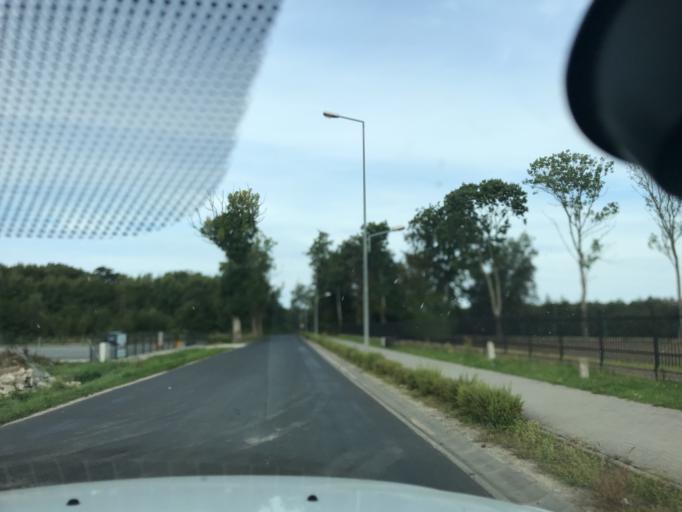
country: PL
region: West Pomeranian Voivodeship
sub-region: Powiat slawienski
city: Darlowo
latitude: 54.5346
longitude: 16.5748
